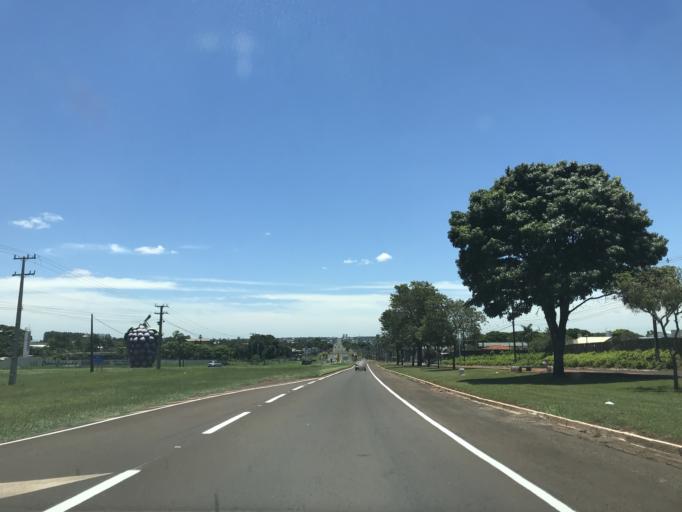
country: BR
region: Parana
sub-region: Marialva
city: Marialva
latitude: -23.4716
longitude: -51.8191
